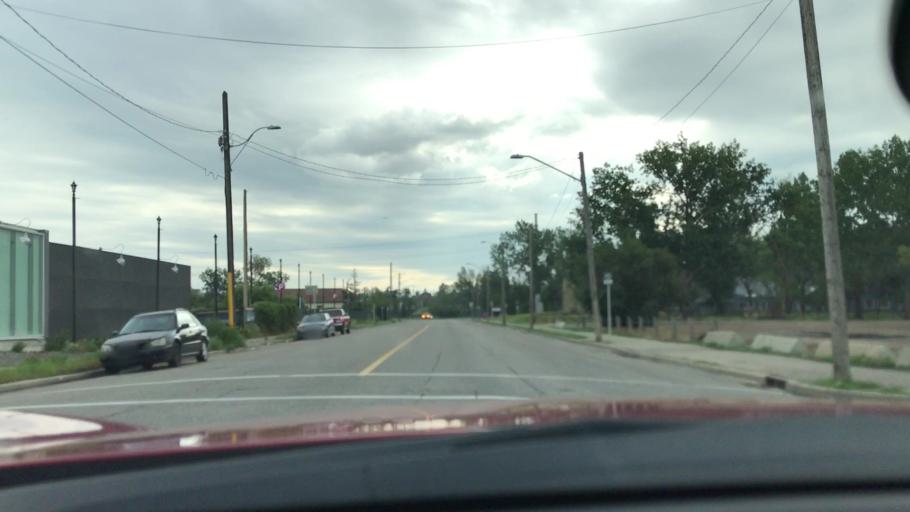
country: CA
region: Alberta
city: Calgary
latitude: 51.0410
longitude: -114.0511
